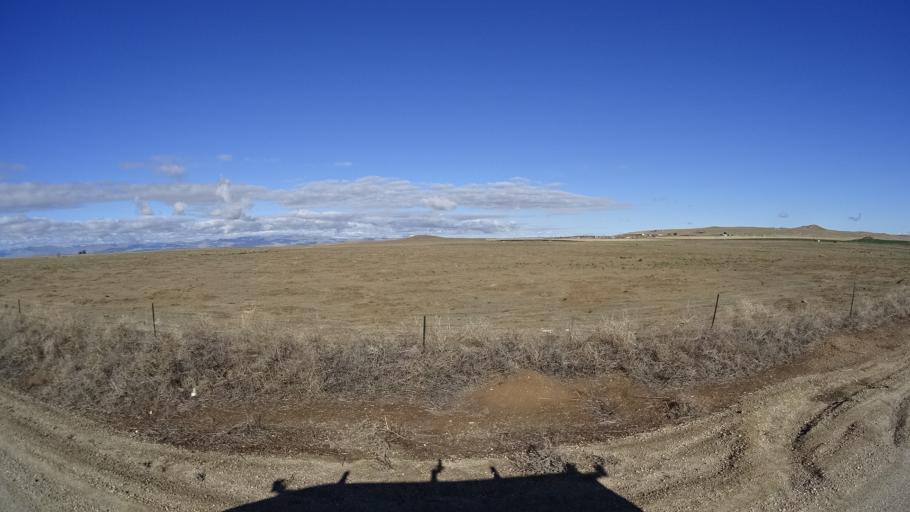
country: US
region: Idaho
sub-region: Ada County
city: Kuna
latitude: 43.4178
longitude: -116.4140
